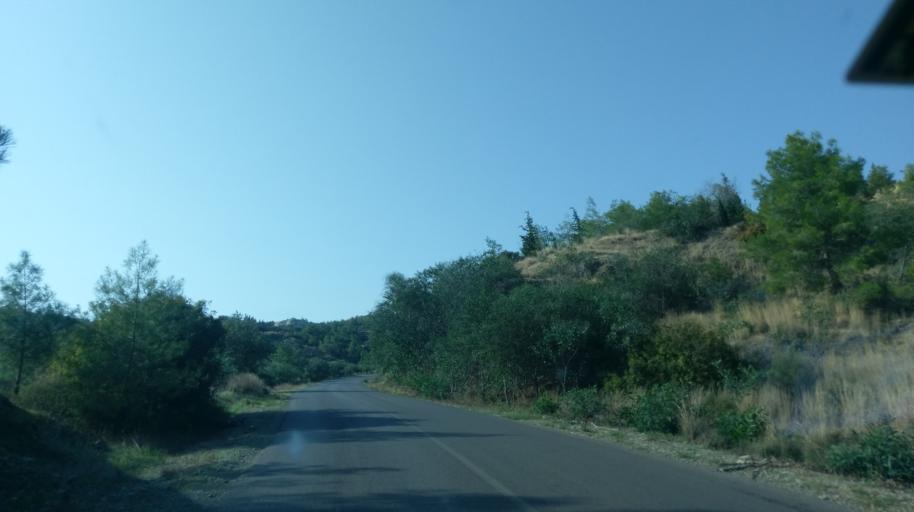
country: CY
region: Lefkosia
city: Lefka
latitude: 35.1536
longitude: 32.7733
